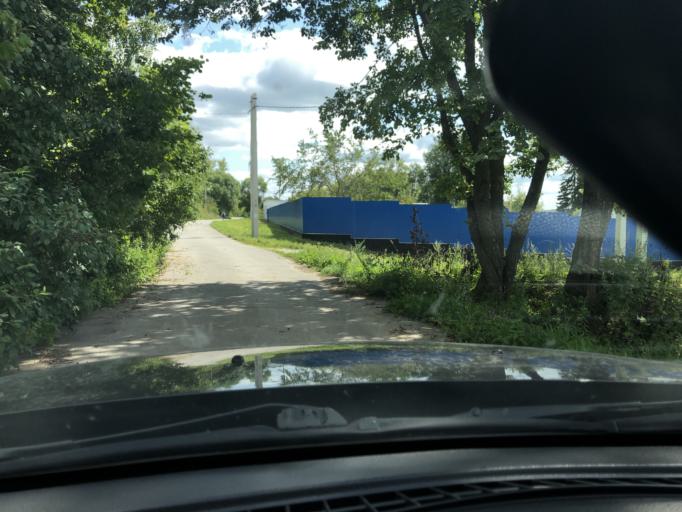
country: RU
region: Tula
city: Revyakino
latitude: 54.3483
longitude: 37.6164
